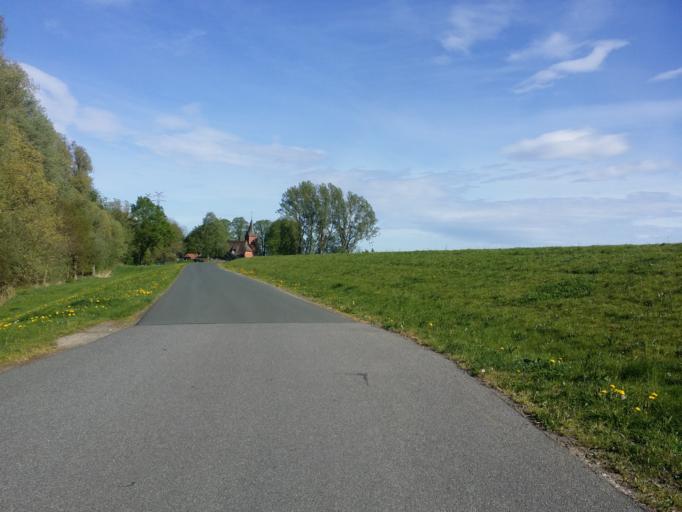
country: DE
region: Lower Saxony
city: Lemwerder
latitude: 53.1295
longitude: 8.6495
